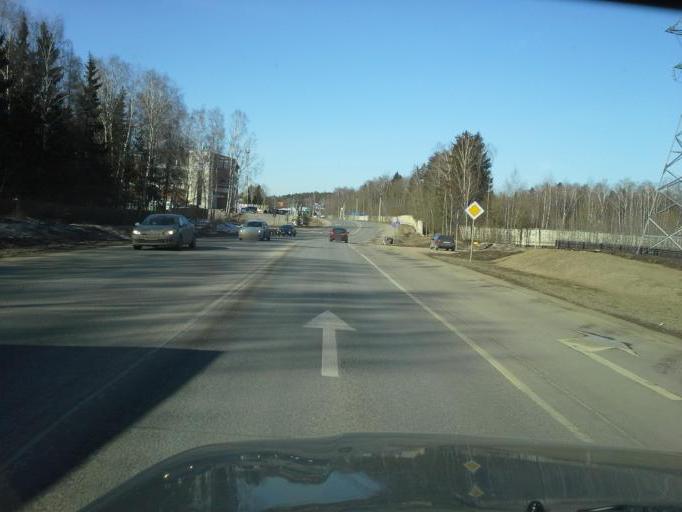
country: RU
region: Moskovskaya
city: Gorki Vtoryye
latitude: 55.6815
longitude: 37.1472
